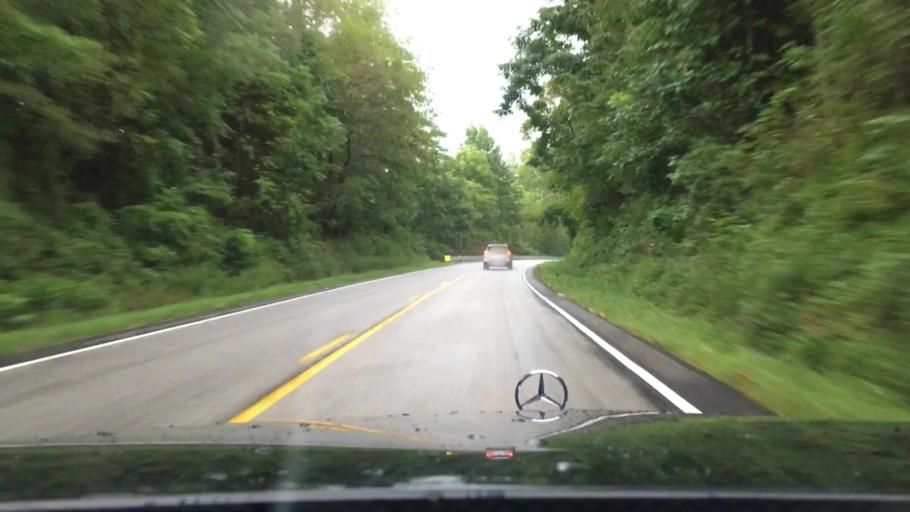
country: US
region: Virginia
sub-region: Amherst County
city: Amherst
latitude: 37.6761
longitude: -79.0167
